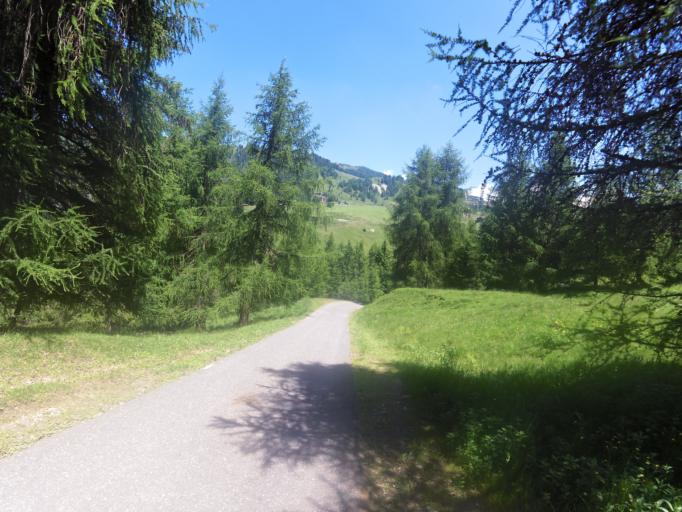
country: IT
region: Trentino-Alto Adige
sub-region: Bolzano
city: Siusi
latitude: 46.5368
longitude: 11.6032
